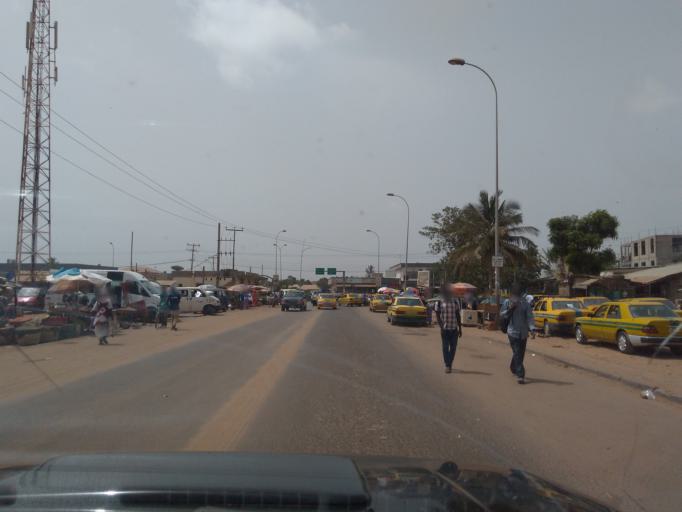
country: GM
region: Western
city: Sukuta
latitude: 13.4345
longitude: -16.6916
